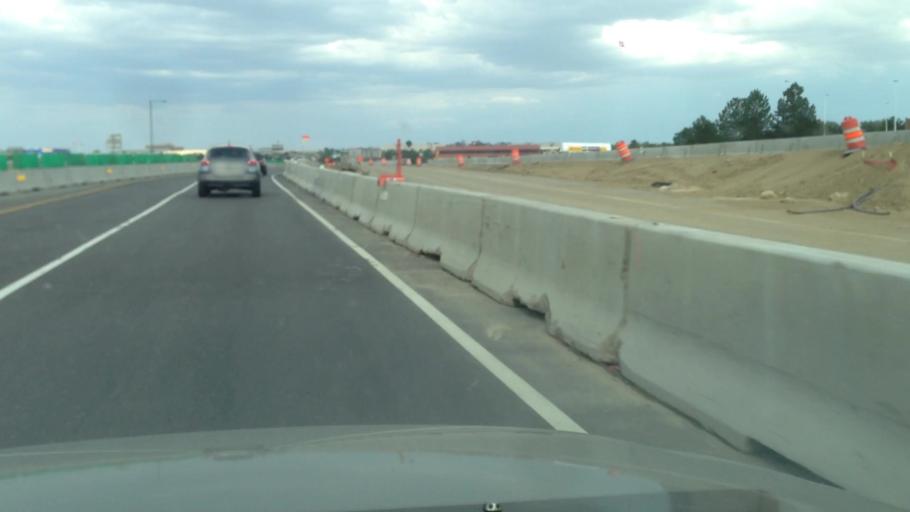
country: US
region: Colorado
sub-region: Douglas County
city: Acres Green
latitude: 39.5638
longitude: -104.9018
